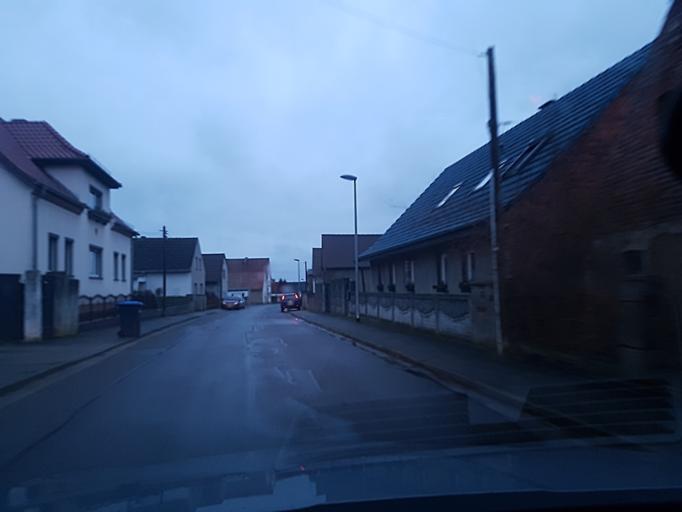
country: DE
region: Brandenburg
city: Bad Liebenwerda
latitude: 51.5408
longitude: 13.4526
